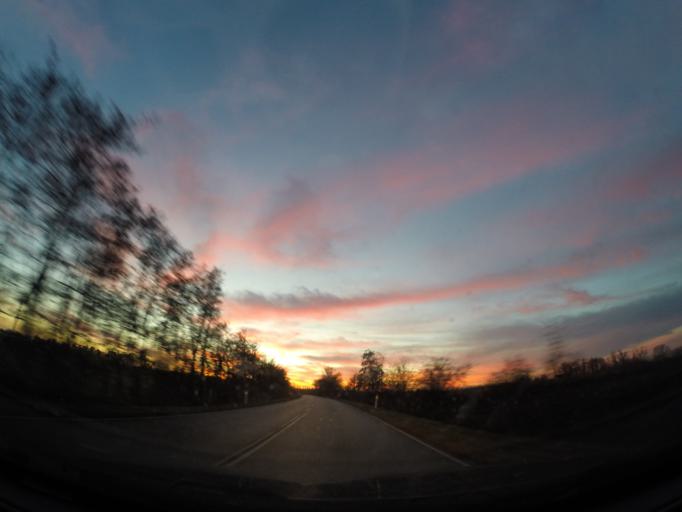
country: DK
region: Capital Region
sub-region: Hoje-Taastrup Kommune
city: Taastrup
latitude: 55.6731
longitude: 12.3002
